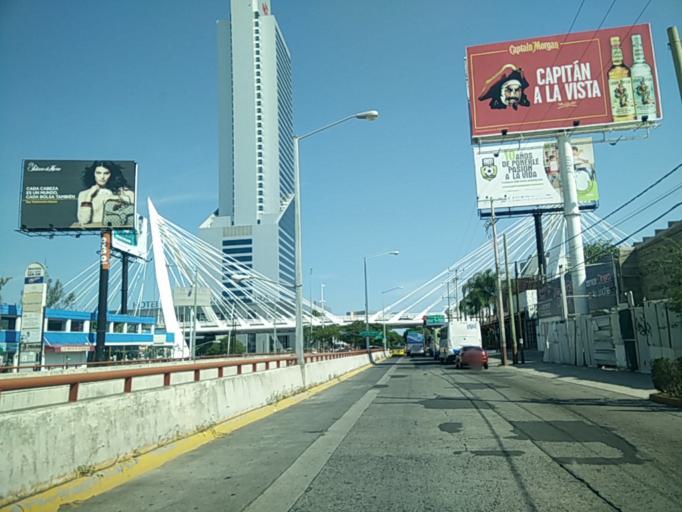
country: MX
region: Jalisco
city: Guadalajara
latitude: 20.6637
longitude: -103.3944
